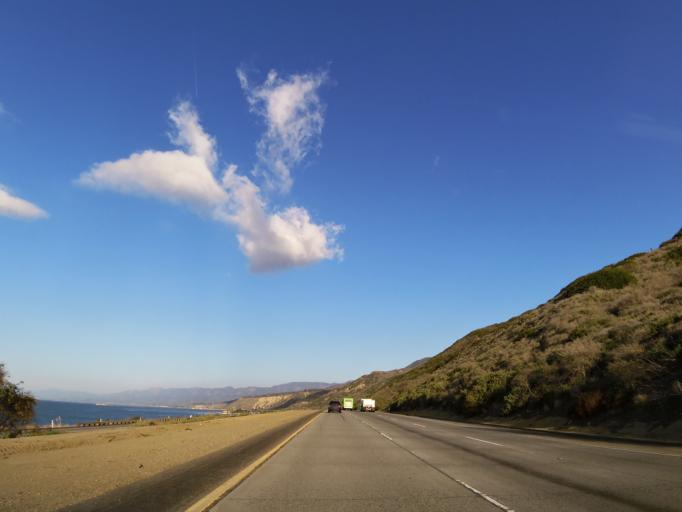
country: US
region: California
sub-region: Ventura County
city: Ventura
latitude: 34.3244
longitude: -119.3929
